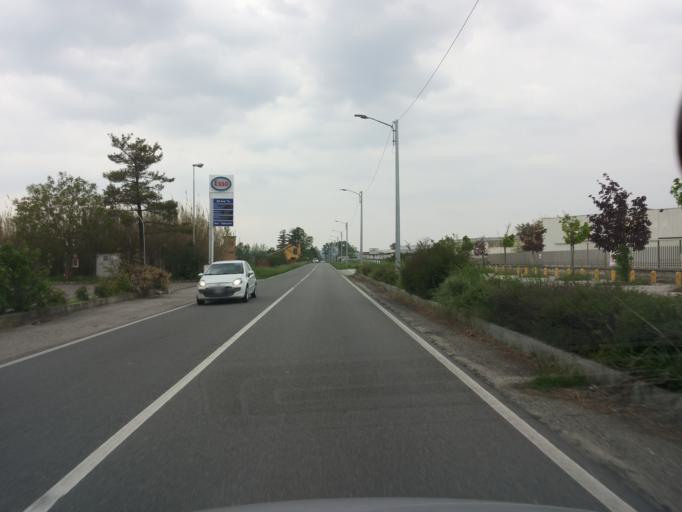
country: IT
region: Piedmont
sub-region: Provincia di Alessandria
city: Occimiano
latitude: 45.0692
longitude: 8.4941
